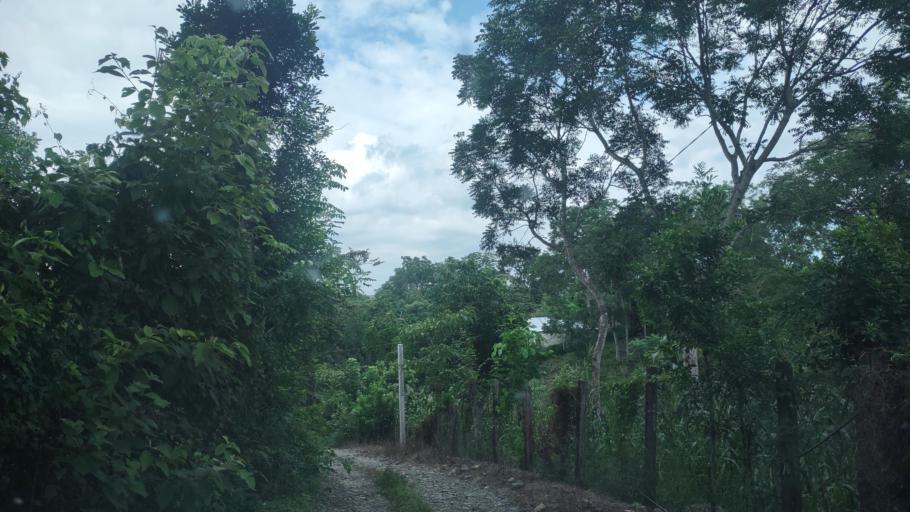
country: MX
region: Veracruz
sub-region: Ixcatepec
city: Ixcatepec
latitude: 21.2138
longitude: -97.9836
